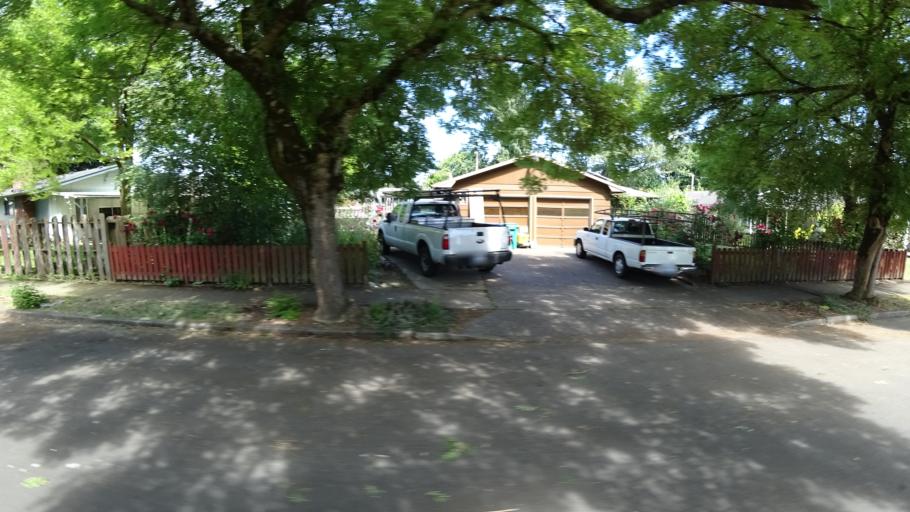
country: US
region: Washington
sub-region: Clark County
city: Vancouver
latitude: 45.5888
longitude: -122.7078
